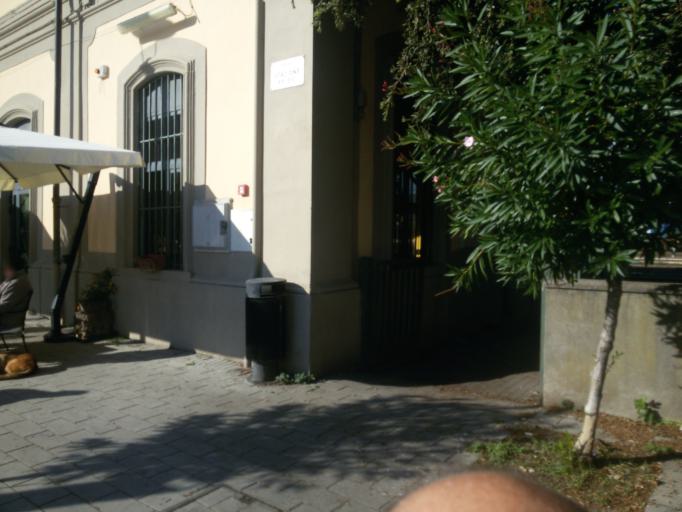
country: IT
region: Liguria
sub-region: Provincia di La Spezia
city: Santo Stefano di Magra
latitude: 44.1570
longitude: 9.9156
